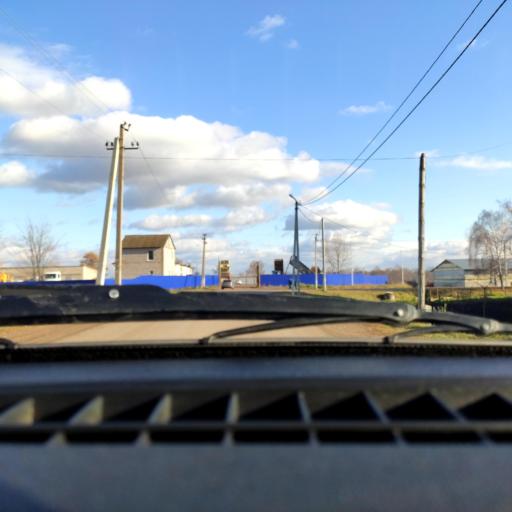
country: RU
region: Bashkortostan
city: Mikhaylovka
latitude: 54.7813
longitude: 55.8403
